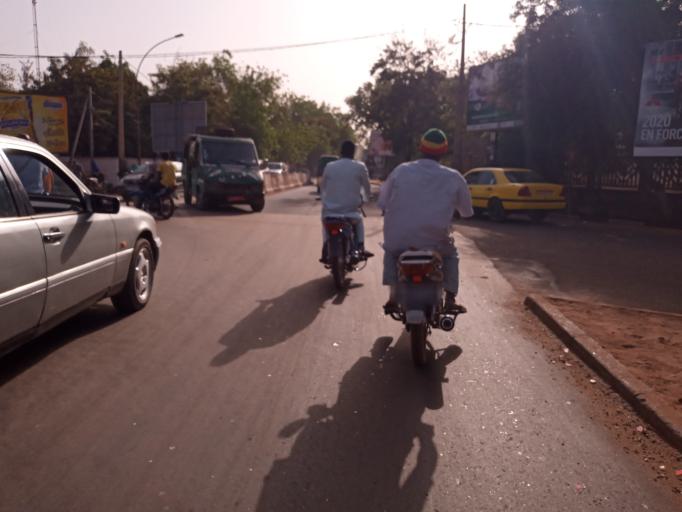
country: ML
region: Bamako
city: Bamako
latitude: 12.6576
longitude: -7.9988
